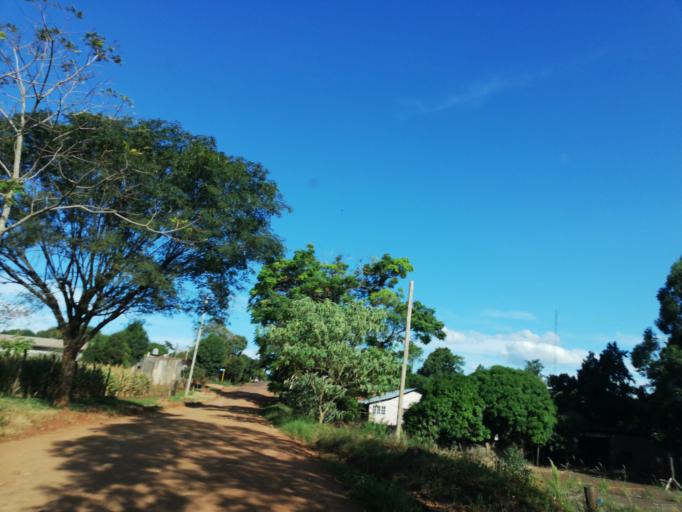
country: AR
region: Misiones
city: Dos de Mayo
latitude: -26.9922
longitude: -54.4958
